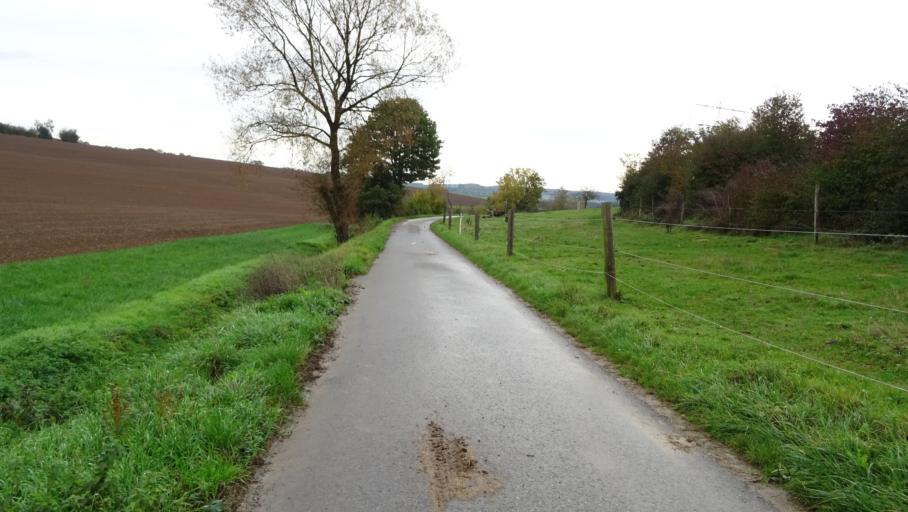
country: DE
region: Baden-Wuerttemberg
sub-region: Karlsruhe Region
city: Billigheim
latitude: 49.3452
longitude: 9.2119
